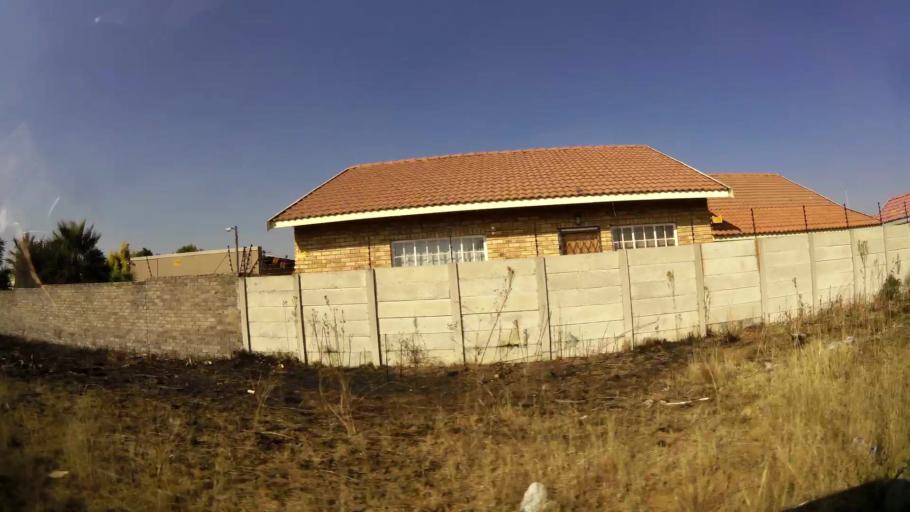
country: ZA
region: Gauteng
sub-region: West Rand District Municipality
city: Randfontein
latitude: -26.1825
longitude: 27.6776
